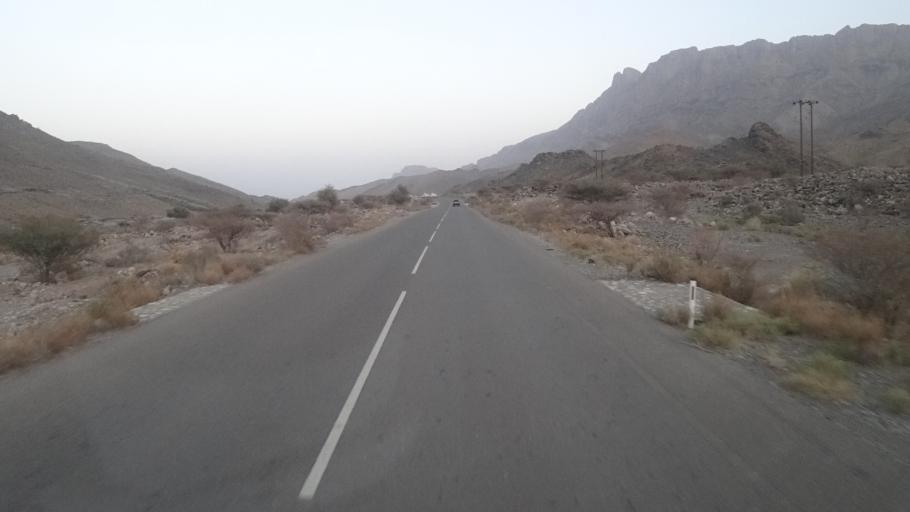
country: OM
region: Muhafazat ad Dakhiliyah
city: Bahla'
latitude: 23.1643
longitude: 57.1621
